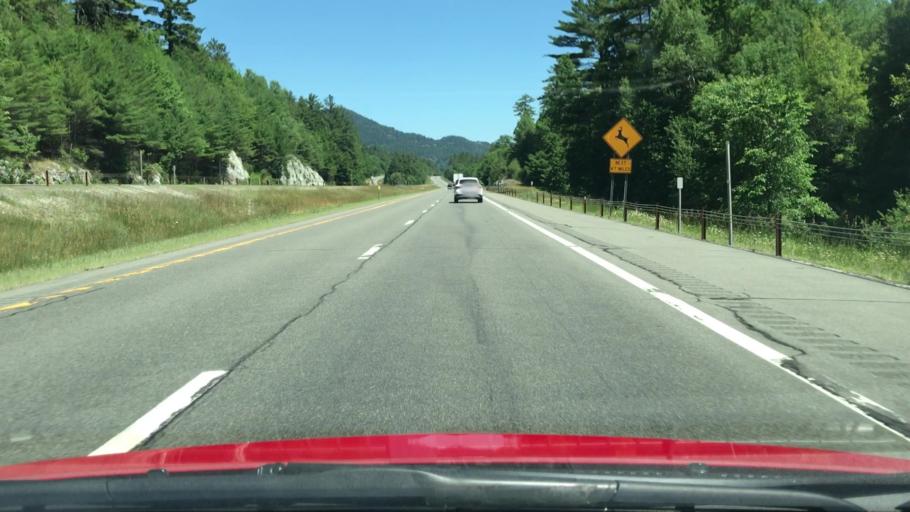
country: US
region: New York
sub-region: Essex County
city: Mineville
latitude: 43.9659
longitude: -73.7268
